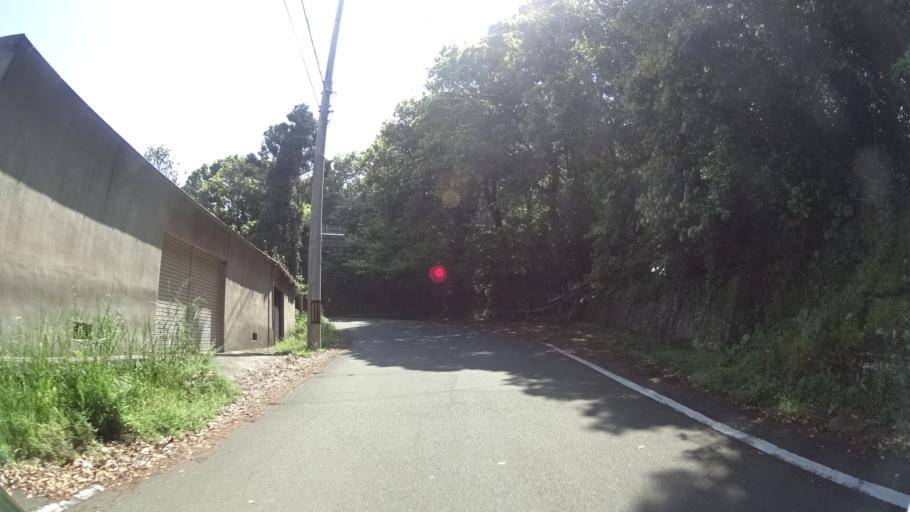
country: JP
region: Ehime
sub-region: Nishiuwa-gun
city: Ikata-cho
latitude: 33.3752
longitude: 132.0570
